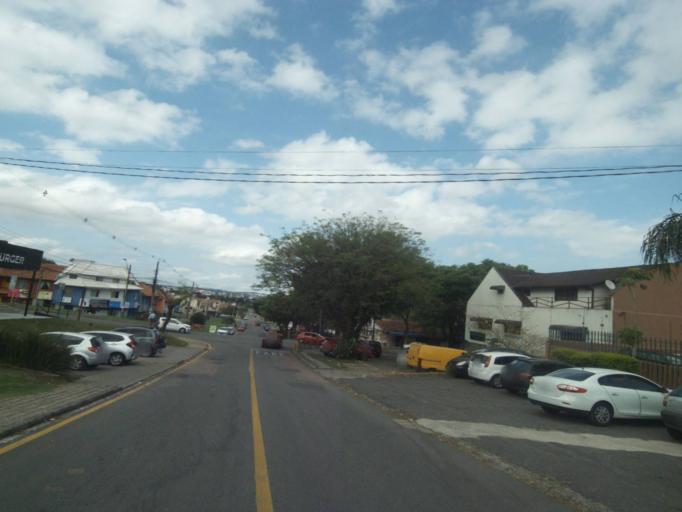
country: BR
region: Parana
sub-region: Pinhais
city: Pinhais
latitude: -25.4140
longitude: -49.2061
